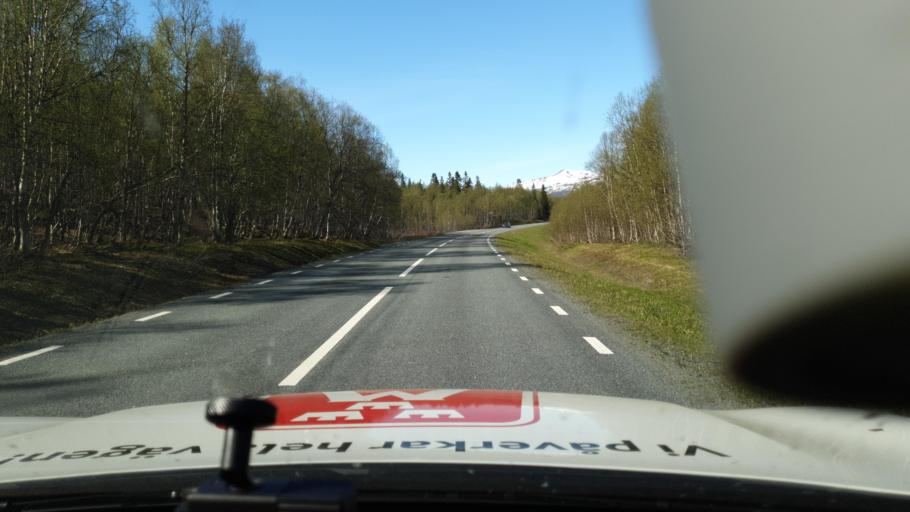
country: NO
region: Nordland
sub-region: Rana
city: Mo i Rana
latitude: 65.7679
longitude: 15.1130
